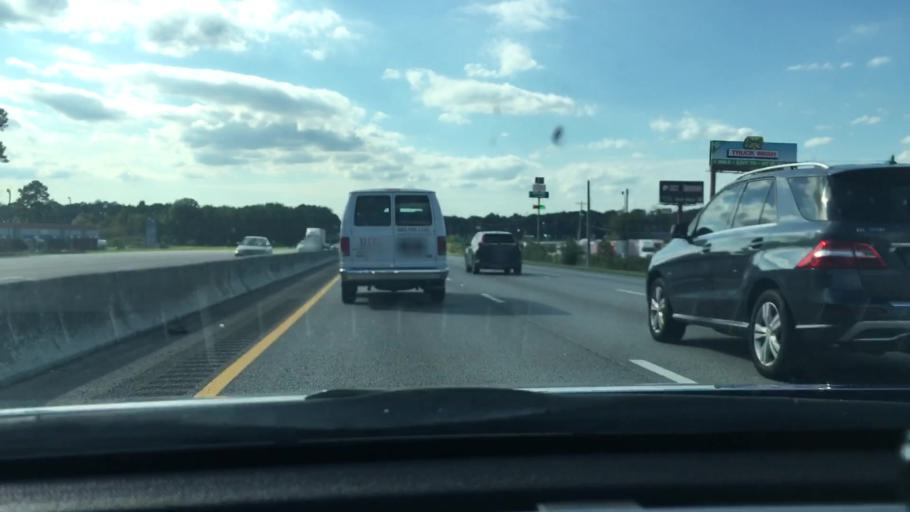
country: US
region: South Carolina
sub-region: Richland County
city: Dentsville
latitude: 34.0735
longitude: -80.9940
